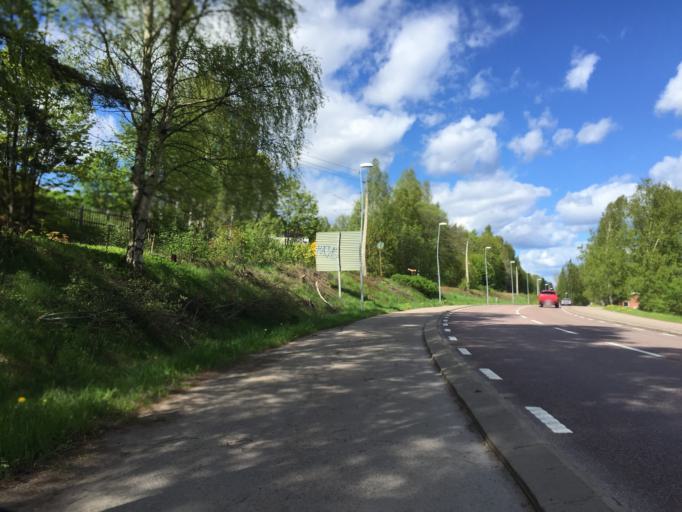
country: SE
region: Dalarna
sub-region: Ludvika Kommun
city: Ludvika
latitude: 60.1561
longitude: 15.1890
